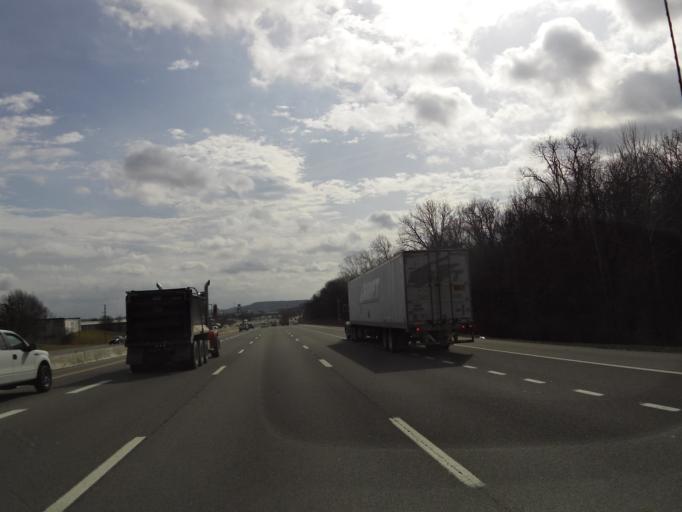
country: US
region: Tennessee
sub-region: Rutherford County
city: La Vergne
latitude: 36.0198
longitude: -86.6268
